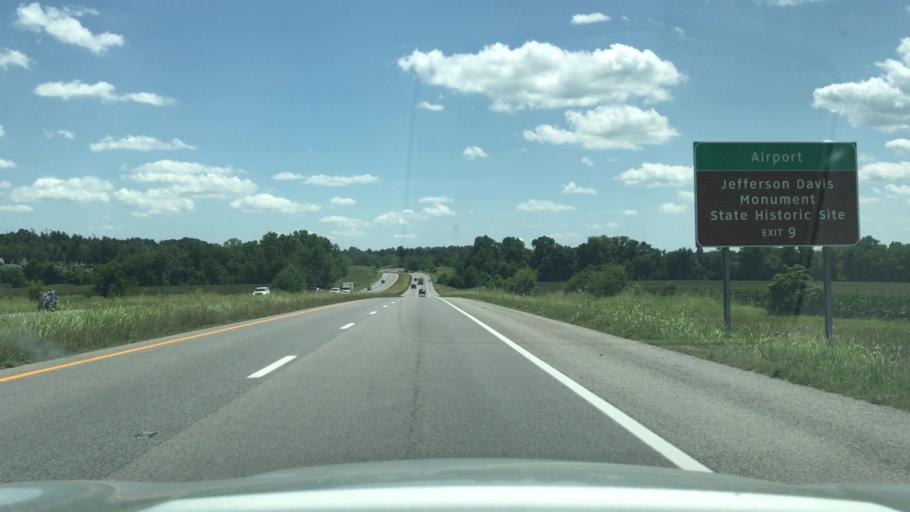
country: US
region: Kentucky
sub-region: Christian County
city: Hopkinsville
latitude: 36.8850
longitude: -87.4688
